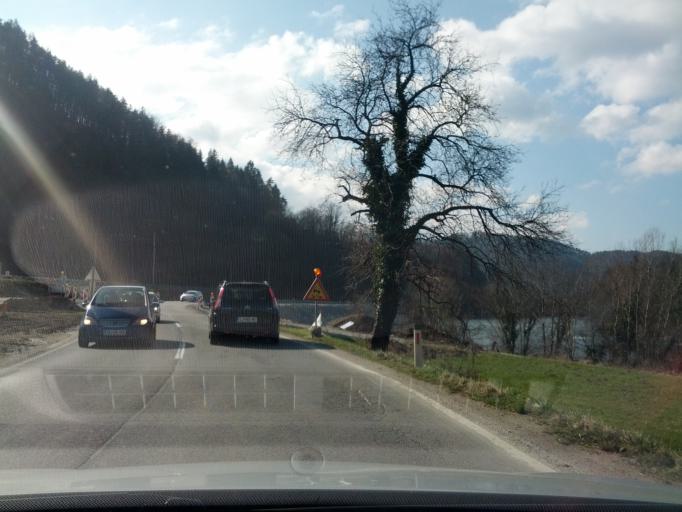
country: SI
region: Litija
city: Litija
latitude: 46.0739
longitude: 14.8224
